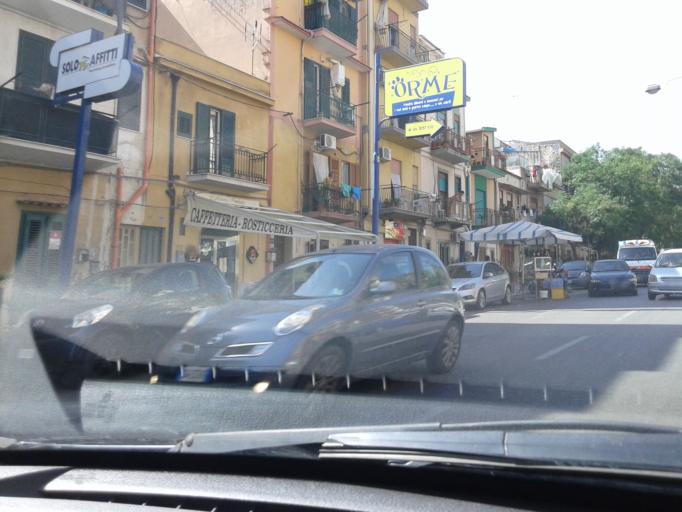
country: IT
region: Sicily
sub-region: Palermo
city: Monreale
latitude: 38.0967
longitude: 13.3146
